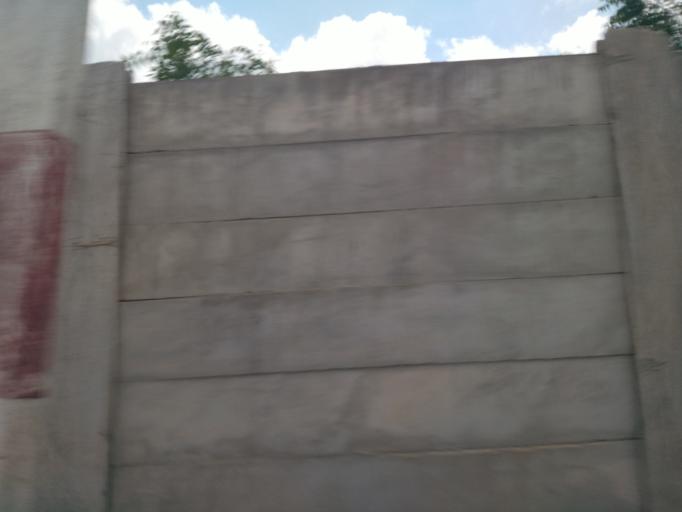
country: TZ
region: Dar es Salaam
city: Dar es Salaam
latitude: -6.8536
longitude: 39.3591
